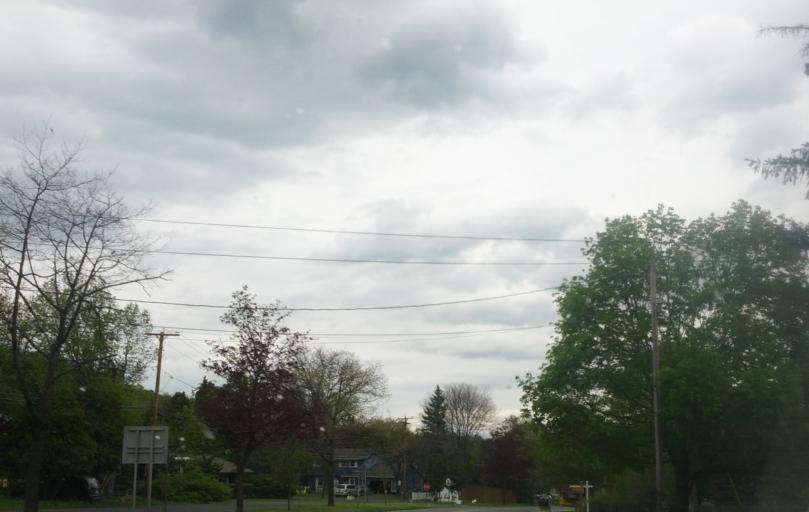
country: US
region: New York
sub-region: Onondaga County
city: Manlius
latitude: 42.9940
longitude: -75.9917
